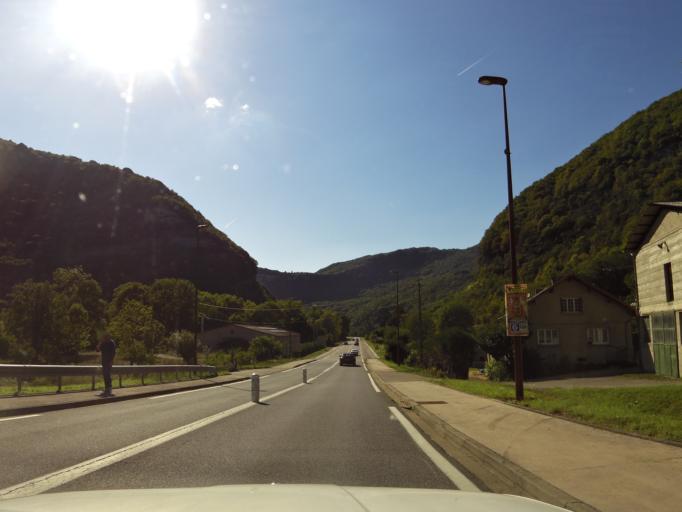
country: FR
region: Rhone-Alpes
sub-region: Departement de l'Ain
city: Saint-Rambert-en-Bugey
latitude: 45.9360
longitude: 5.4242
